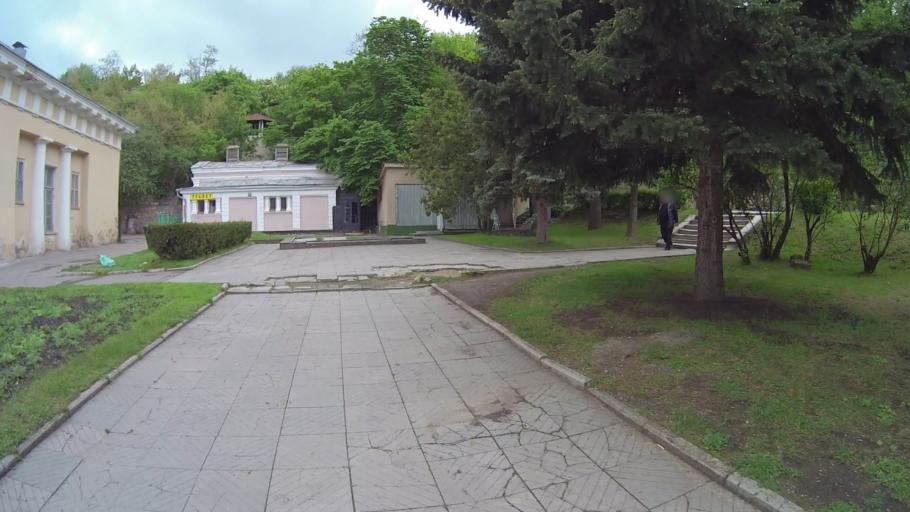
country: RU
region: Stavropol'skiy
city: Goryachevodskiy
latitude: 44.0361
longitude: 43.0817
